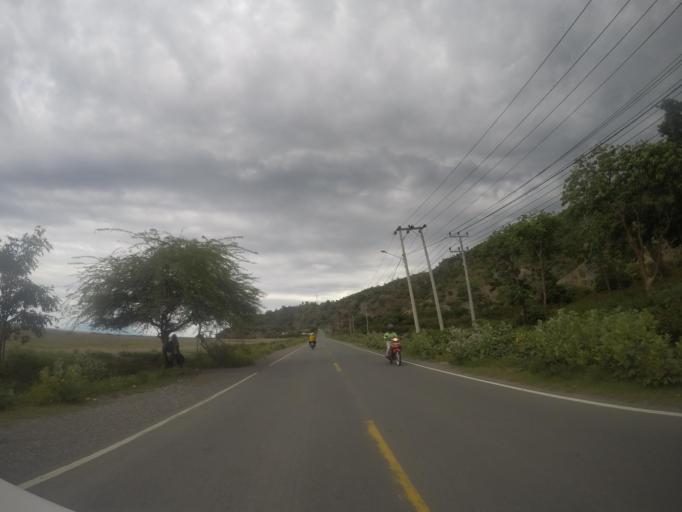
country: TL
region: Liquica
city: Liquica
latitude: -8.5783
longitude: 125.3657
